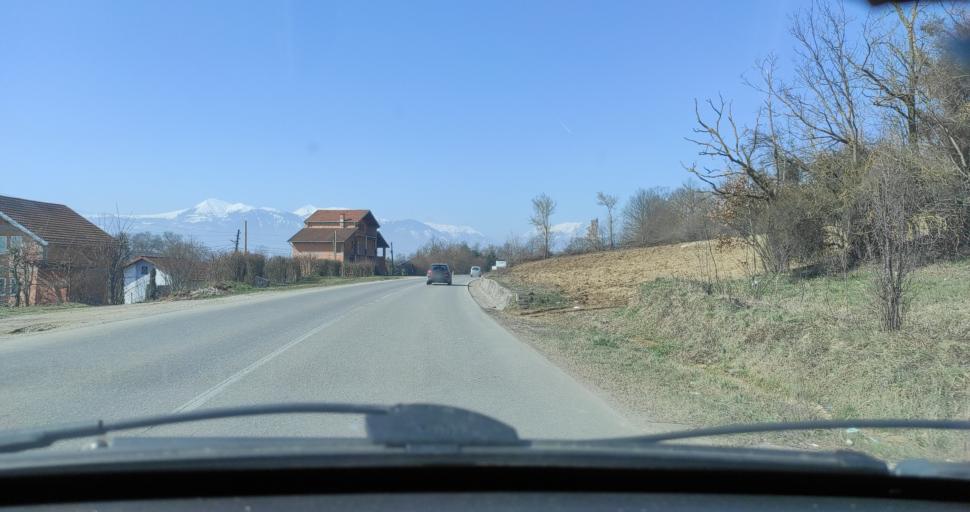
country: XK
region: Pec
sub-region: Komuna e Pejes
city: Kosuriq
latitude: 42.6205
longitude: 20.4801
